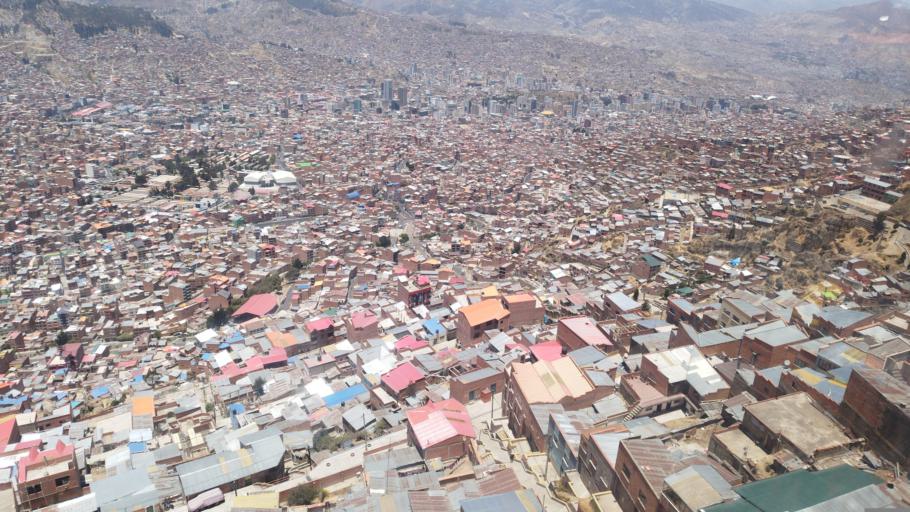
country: BO
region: La Paz
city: La Paz
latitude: -16.5020
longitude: -68.1619
